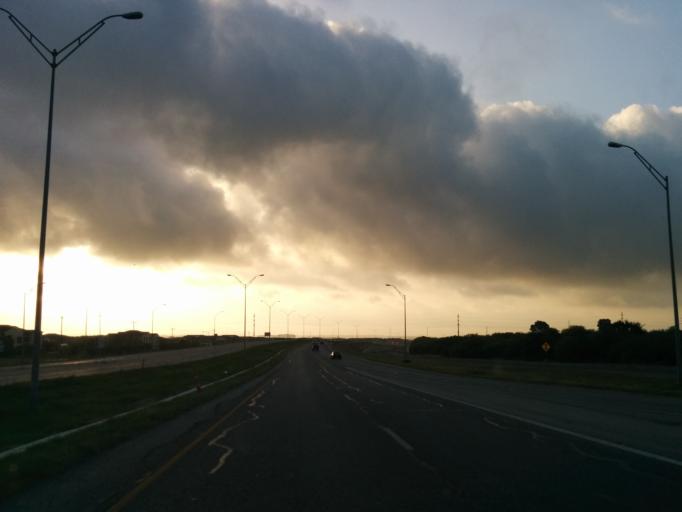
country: US
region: Texas
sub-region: Bexar County
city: Leon Valley
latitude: 29.4464
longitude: -98.6750
